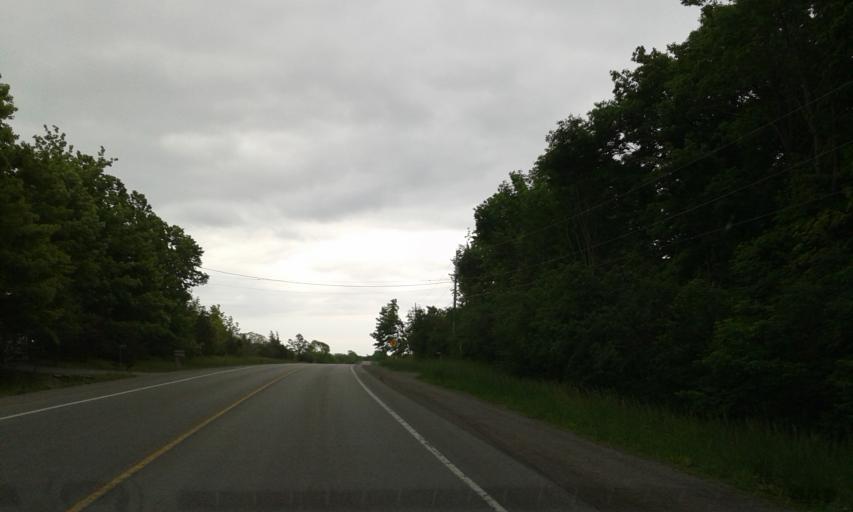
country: CA
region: Ontario
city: Quinte West
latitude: 43.9732
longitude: -77.5043
